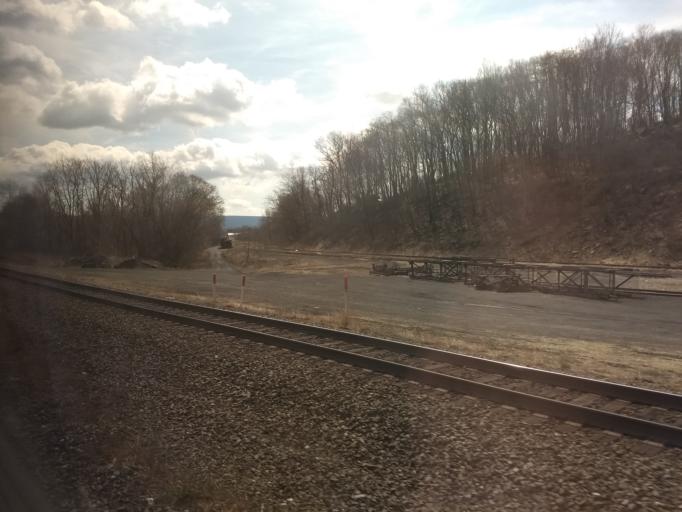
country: US
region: Pennsylvania
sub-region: Huntingdon County
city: Mount Union
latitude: 40.3906
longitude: -77.8919
